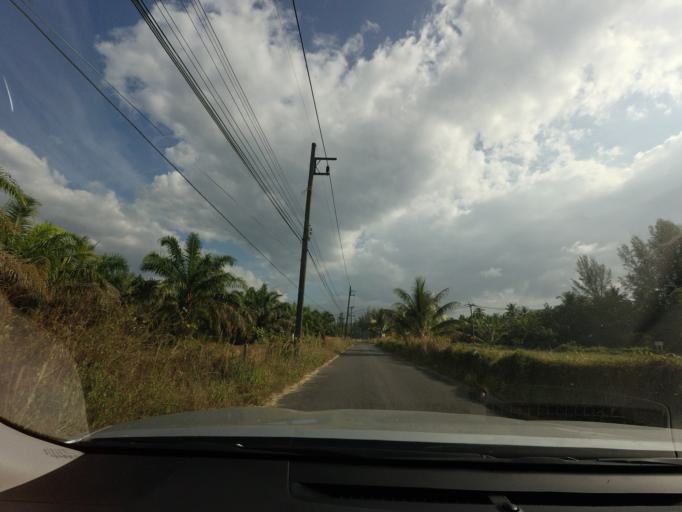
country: TH
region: Phangnga
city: Ban Khao Lak
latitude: 8.7249
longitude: 98.2435
